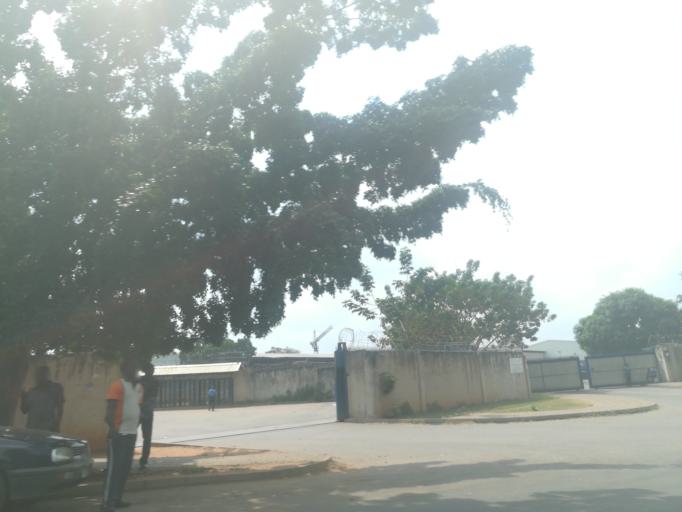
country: NG
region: Abuja Federal Capital Territory
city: Abuja
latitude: 9.0645
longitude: 7.4492
